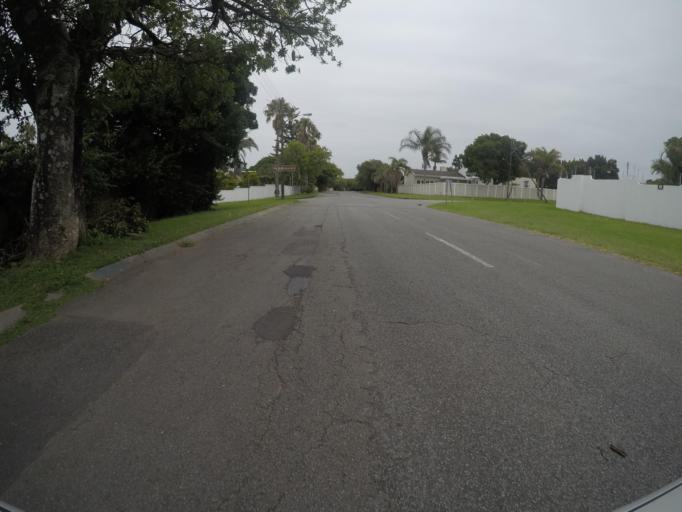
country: ZA
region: Eastern Cape
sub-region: Buffalo City Metropolitan Municipality
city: East London
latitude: -32.9757
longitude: 27.9391
